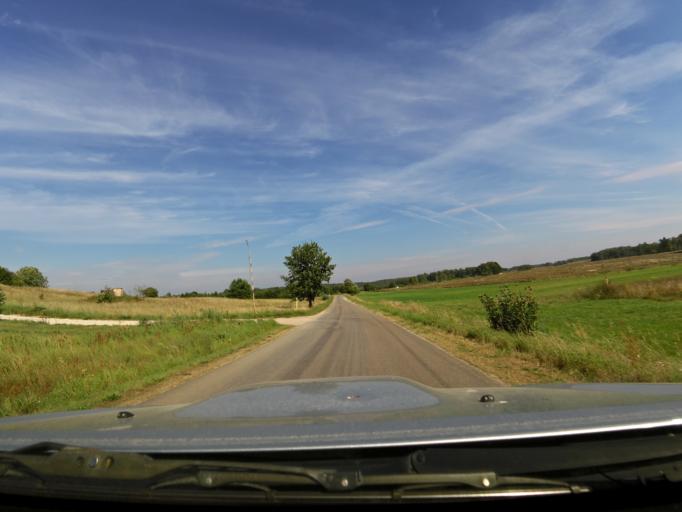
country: LT
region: Vilnius County
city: Pasilaiciai
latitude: 54.8329
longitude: 25.1585
